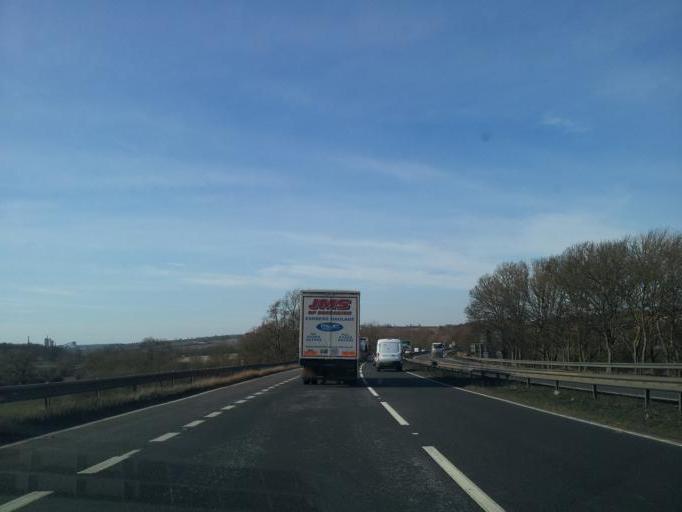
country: GB
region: England
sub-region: Lincolnshire
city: Stamford
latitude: 52.6393
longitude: -0.4935
